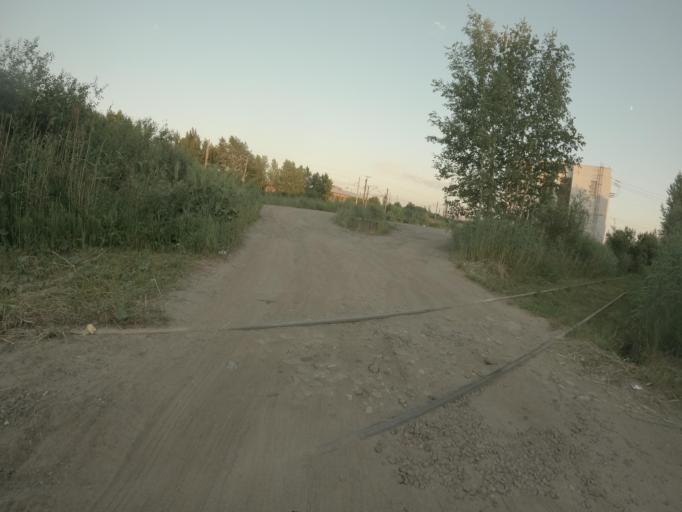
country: RU
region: St.-Petersburg
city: Admiralteisky
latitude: 59.8843
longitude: 30.2932
